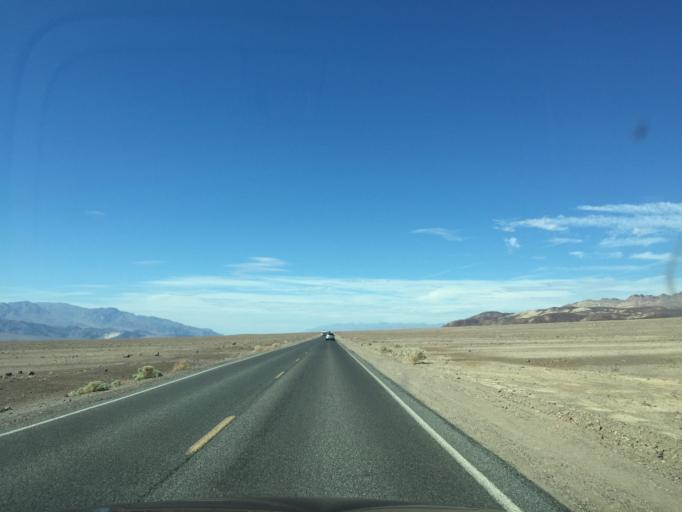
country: US
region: Nevada
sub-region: Nye County
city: Beatty
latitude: 36.2876
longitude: -116.8054
